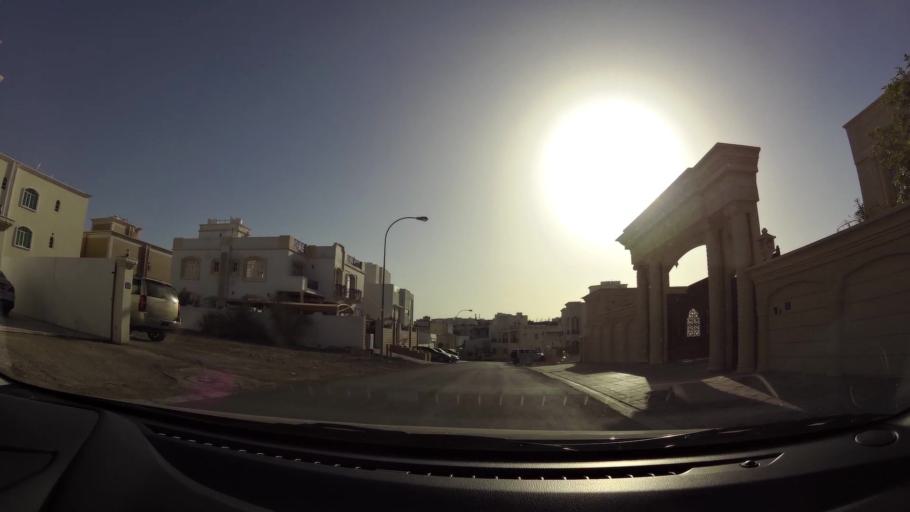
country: OM
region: Muhafazat Masqat
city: As Sib al Jadidah
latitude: 23.6048
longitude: 58.2160
